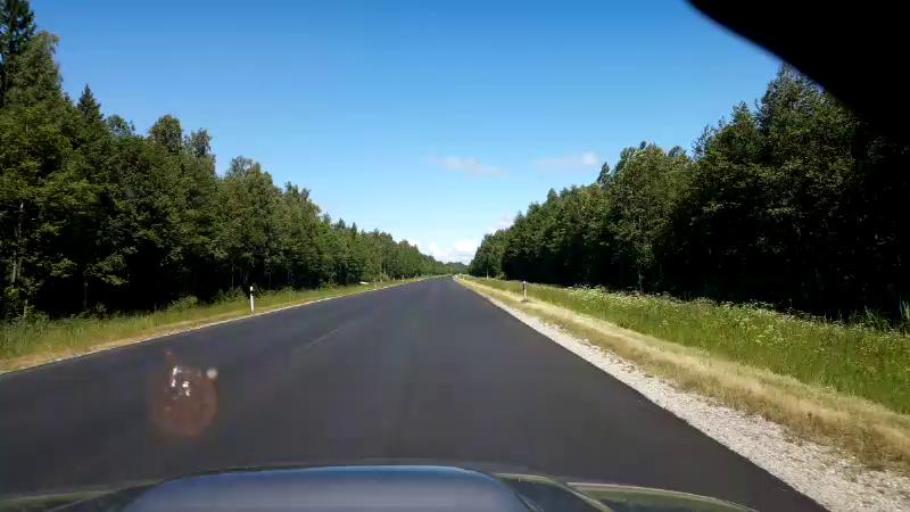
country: LV
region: Salacgrivas
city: Ainazi
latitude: 57.9331
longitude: 24.4276
